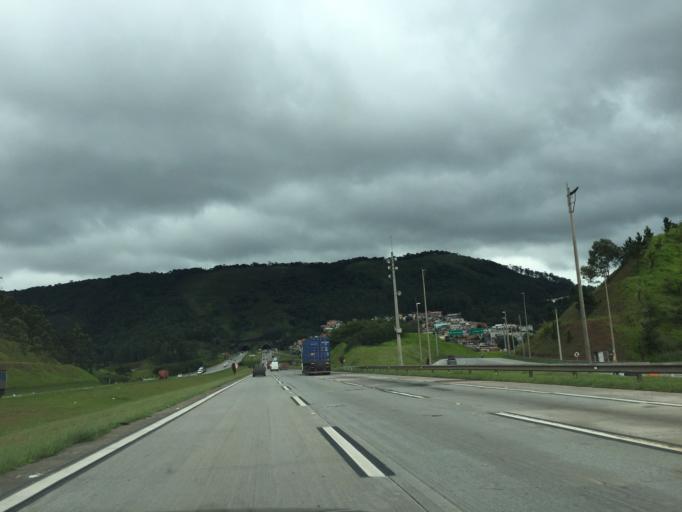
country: BR
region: Sao Paulo
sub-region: Osasco
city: Osasco
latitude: -23.4481
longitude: -46.7820
